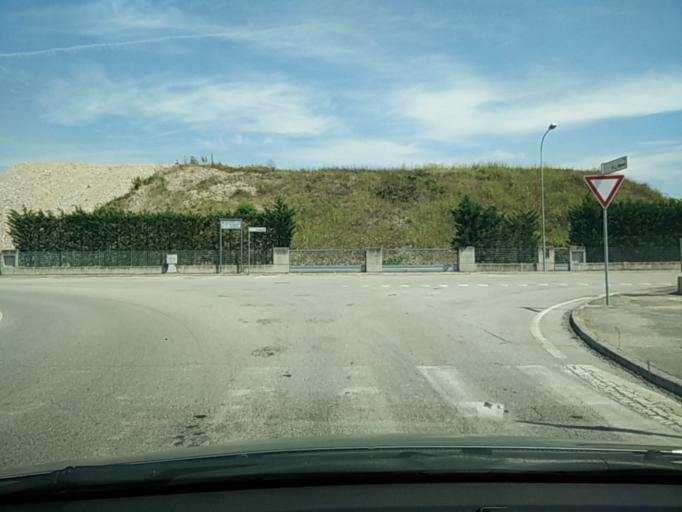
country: IT
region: Veneto
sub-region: Provincia di Venezia
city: Iesolo
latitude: 45.5522
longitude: 12.6567
